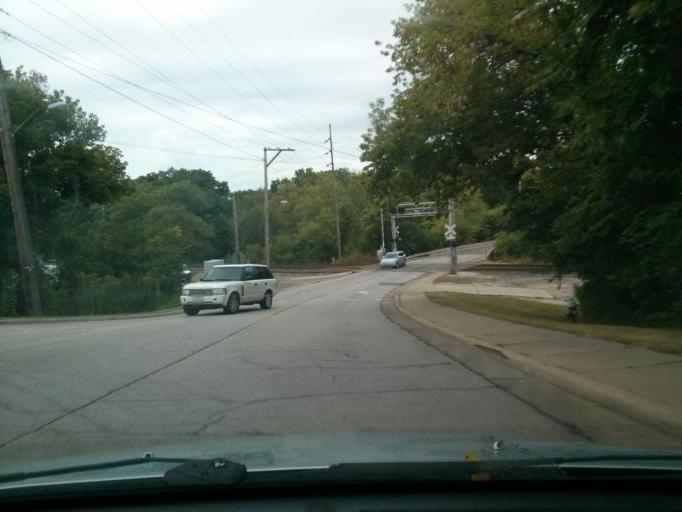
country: US
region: Ohio
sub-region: Portage County
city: Kent
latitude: 41.1501
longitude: -81.3610
